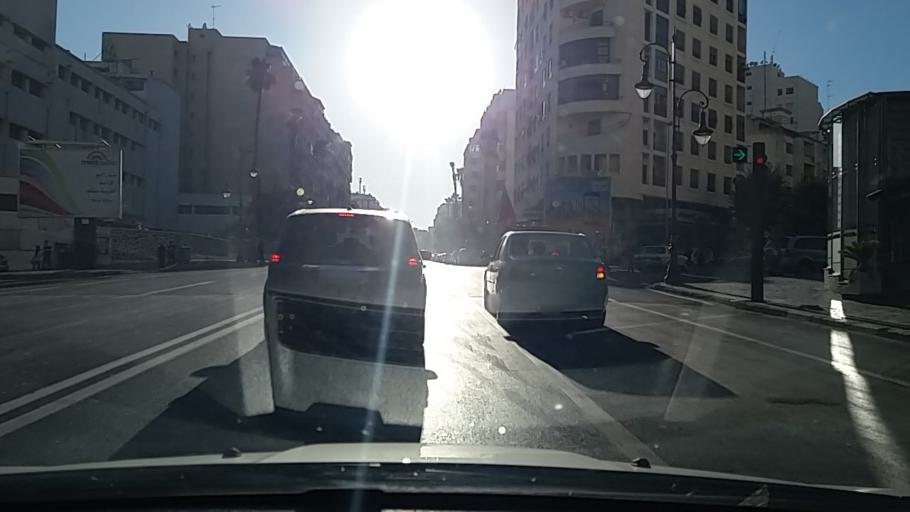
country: MA
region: Tanger-Tetouan
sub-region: Tanger-Assilah
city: Tangier
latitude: 35.7701
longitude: -5.8056
